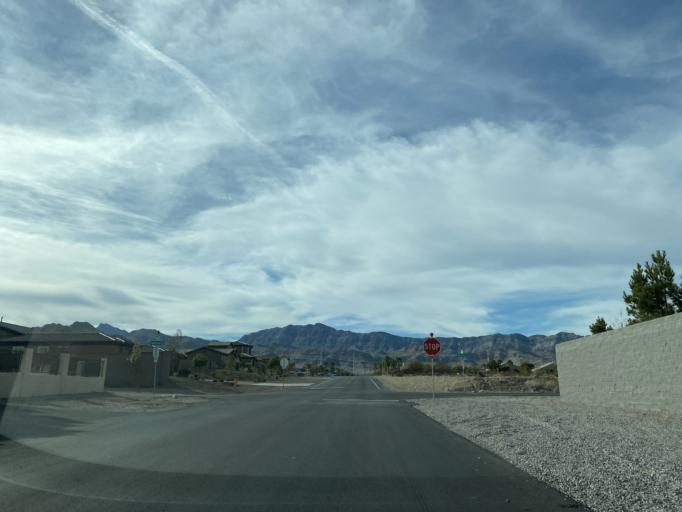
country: US
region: Nevada
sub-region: Clark County
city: Summerlin South
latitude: 36.2700
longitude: -115.3214
